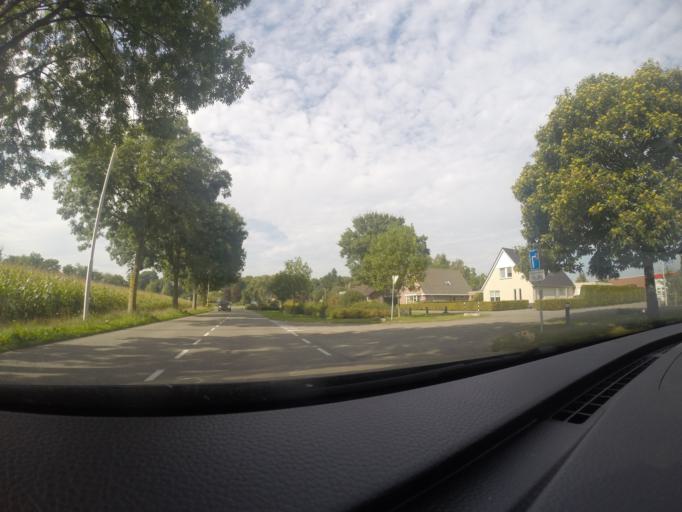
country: NL
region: Gelderland
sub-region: Gemeente Bronckhorst
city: Zelhem
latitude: 51.9990
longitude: 6.3478
